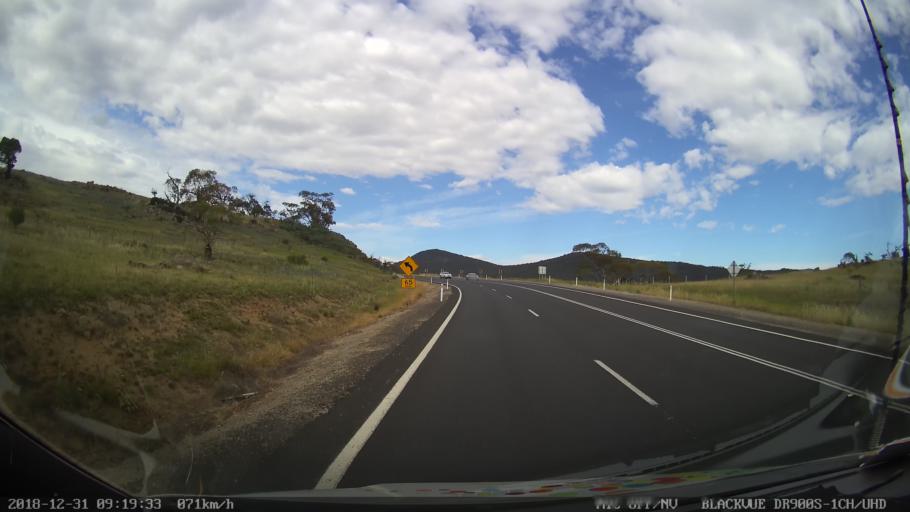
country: AU
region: New South Wales
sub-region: Snowy River
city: Jindabyne
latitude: -36.4160
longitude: 148.5846
